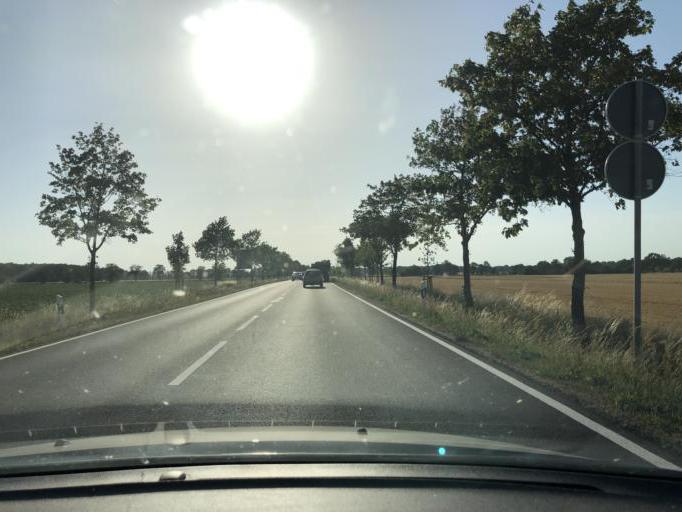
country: DE
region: Saxony
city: Oschatz
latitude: 51.3189
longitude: 13.0642
